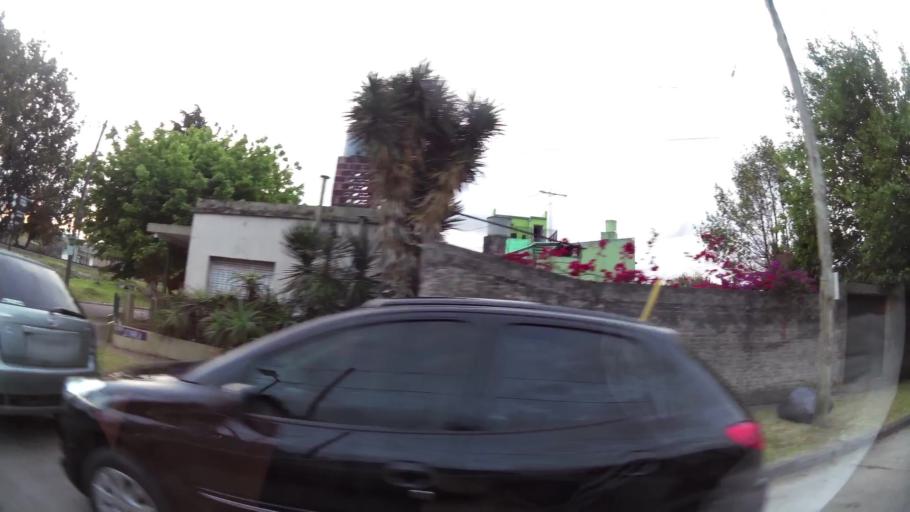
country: AR
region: Buenos Aires
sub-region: Partido de Quilmes
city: Quilmes
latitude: -34.7414
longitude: -58.2452
